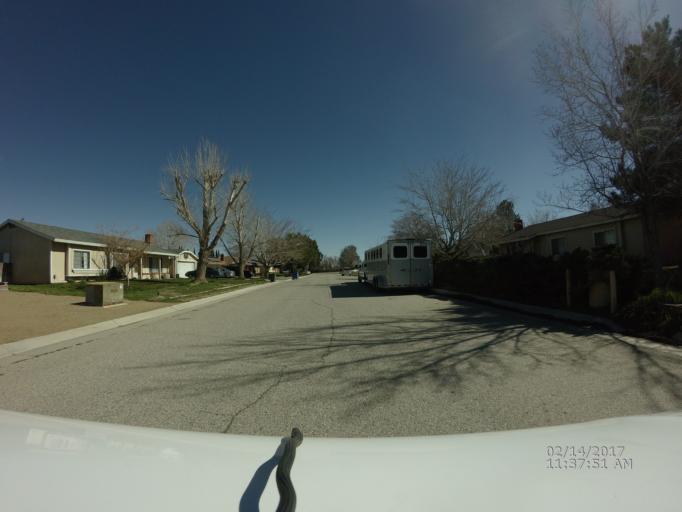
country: US
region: California
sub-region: Los Angeles County
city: Littlerock
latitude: 34.5628
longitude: -117.9537
